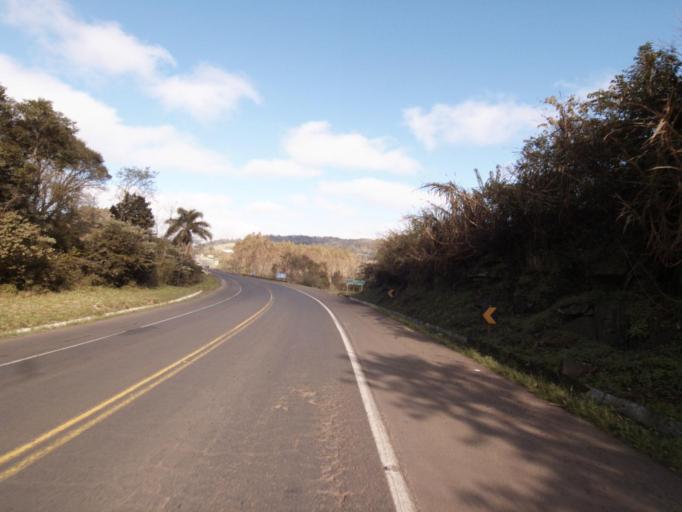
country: BR
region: Rio Grande do Sul
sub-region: Frederico Westphalen
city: Frederico Westphalen
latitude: -27.0672
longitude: -53.2275
